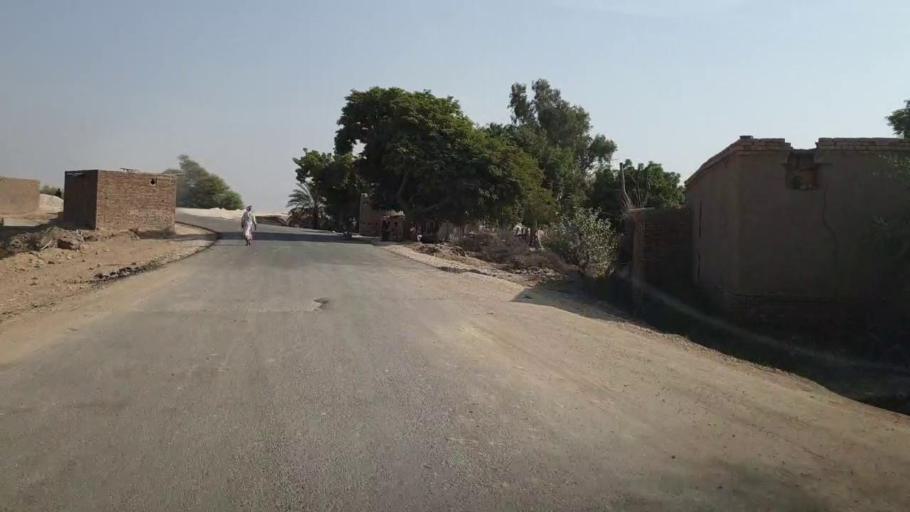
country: PK
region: Sindh
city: Bhan
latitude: 26.5626
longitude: 67.7733
